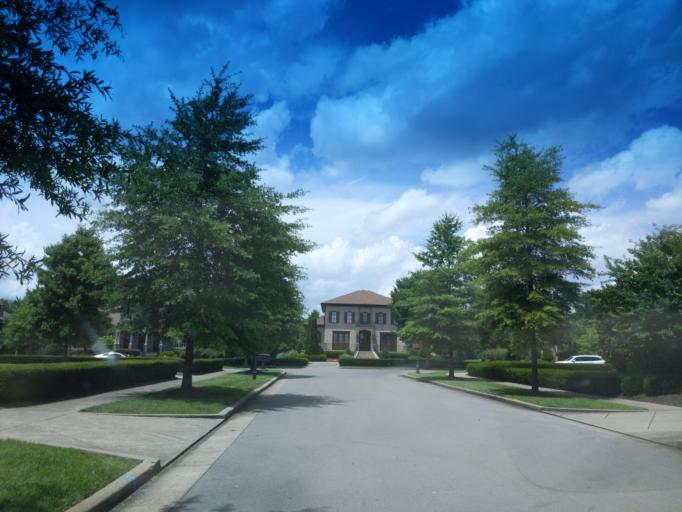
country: US
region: Tennessee
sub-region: Williamson County
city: Brentwood Estates
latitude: 36.0215
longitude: -86.7728
